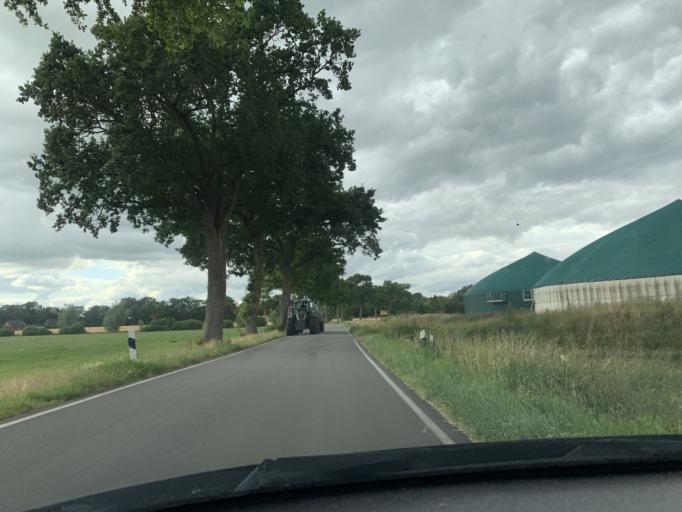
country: DE
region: Lower Saxony
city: Westerstede
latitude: 53.2230
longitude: 7.9039
